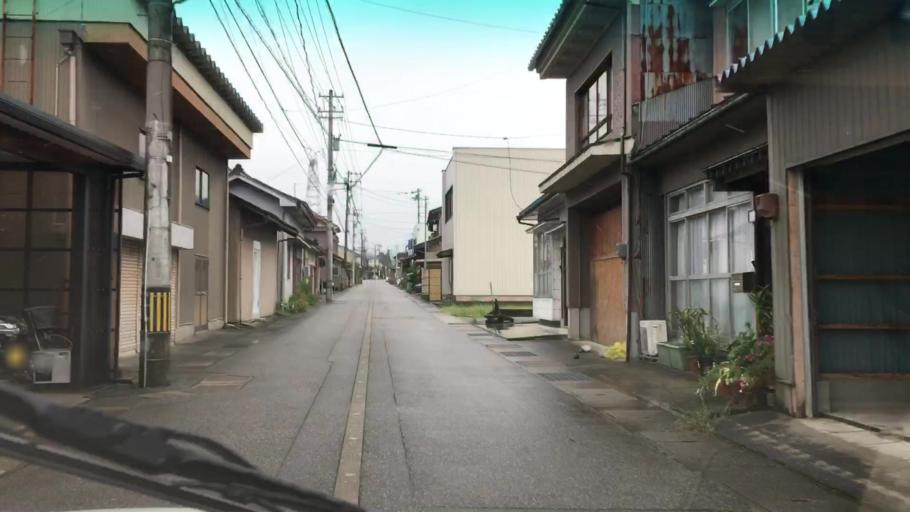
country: JP
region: Toyama
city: Kamiichi
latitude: 36.6550
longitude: 137.3184
